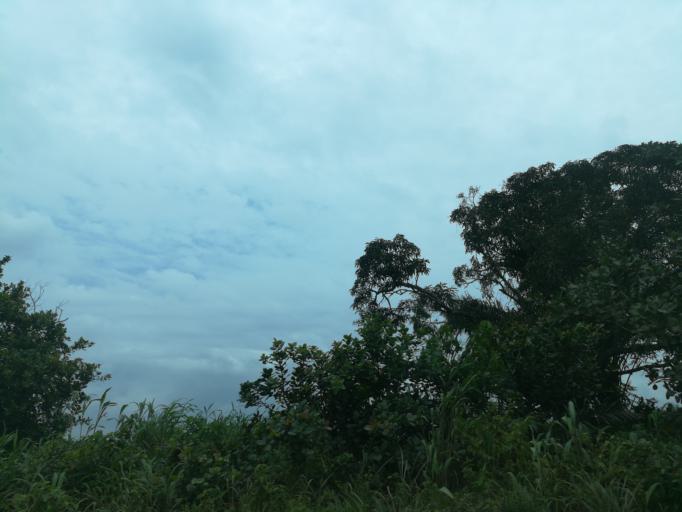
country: NG
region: Lagos
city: Ejirin
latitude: 6.6471
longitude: 3.8346
